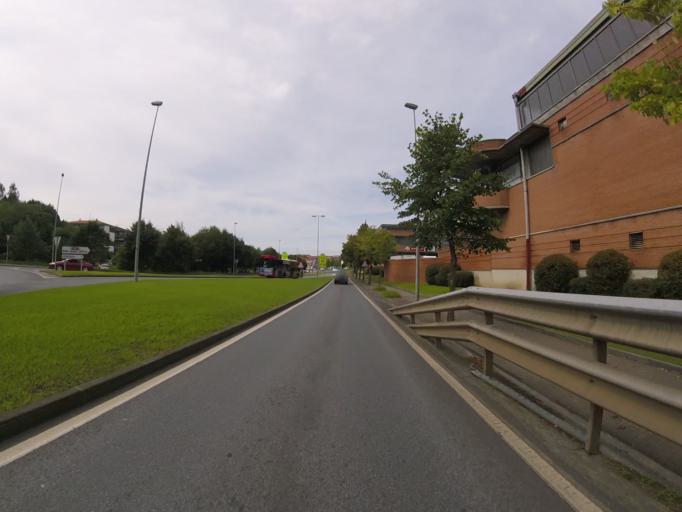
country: ES
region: Basque Country
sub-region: Provincia de Guipuzcoa
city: Irun
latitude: 43.3413
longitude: -1.7584
